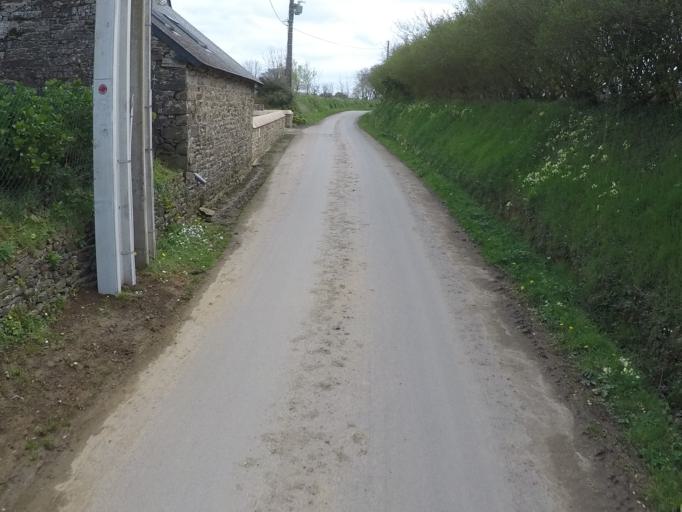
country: FR
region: Brittany
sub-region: Departement des Cotes-d'Armor
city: Plouha
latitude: 48.7111
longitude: -2.9397
